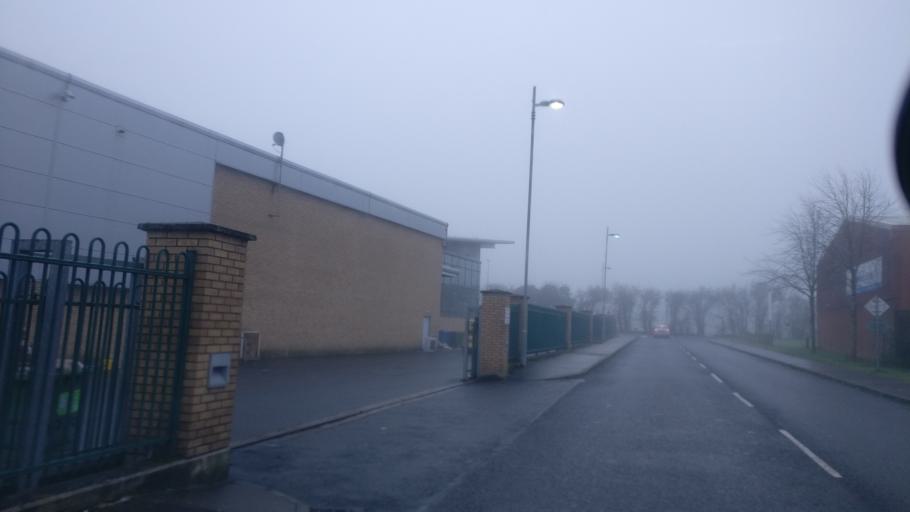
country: IE
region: Munster
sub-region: County Limerick
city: Annacotty
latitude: 52.6490
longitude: -8.5764
